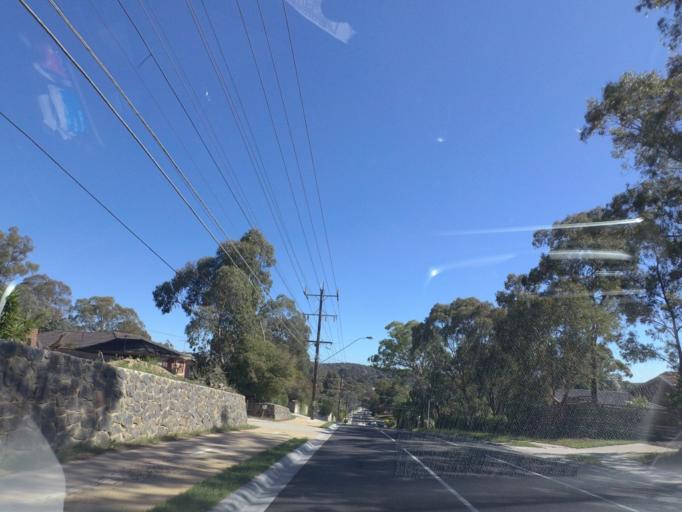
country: AU
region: Victoria
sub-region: Nillumbik
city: Eltham
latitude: -37.7263
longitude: 145.1359
